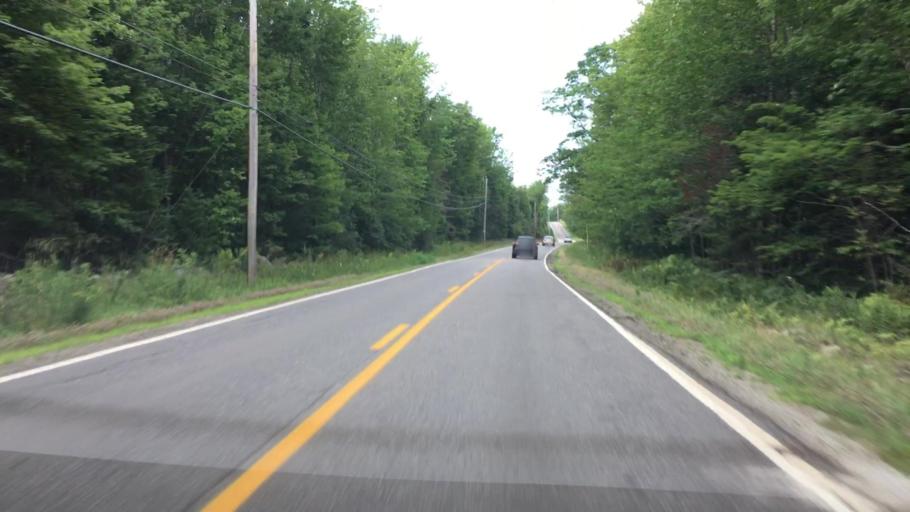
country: US
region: Maine
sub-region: Waldo County
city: Belfast
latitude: 44.3693
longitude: -69.0372
